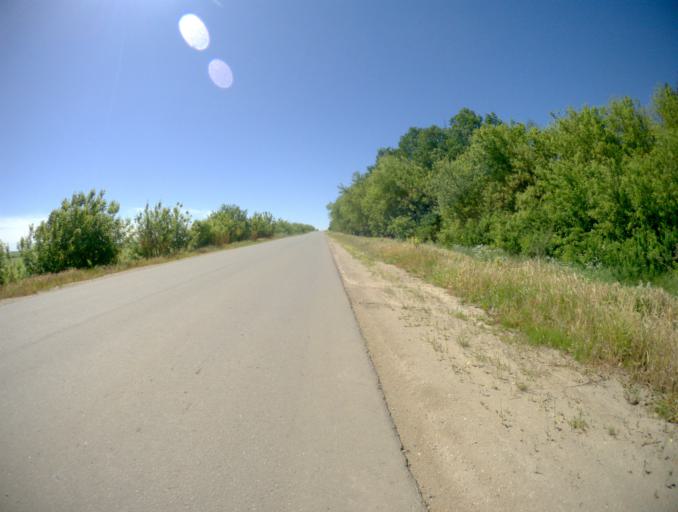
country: RU
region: Ivanovo
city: Gavrilov Posad
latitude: 56.5650
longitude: 40.0378
